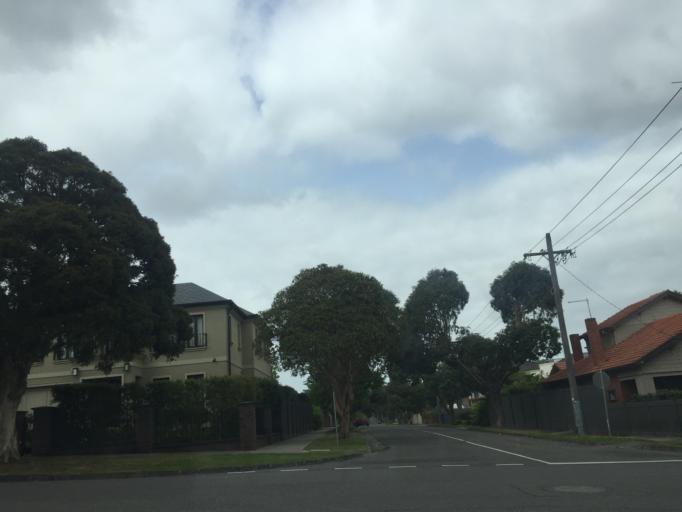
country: AU
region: Victoria
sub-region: Boroondara
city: Kew East
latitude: -37.8035
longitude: 145.0535
